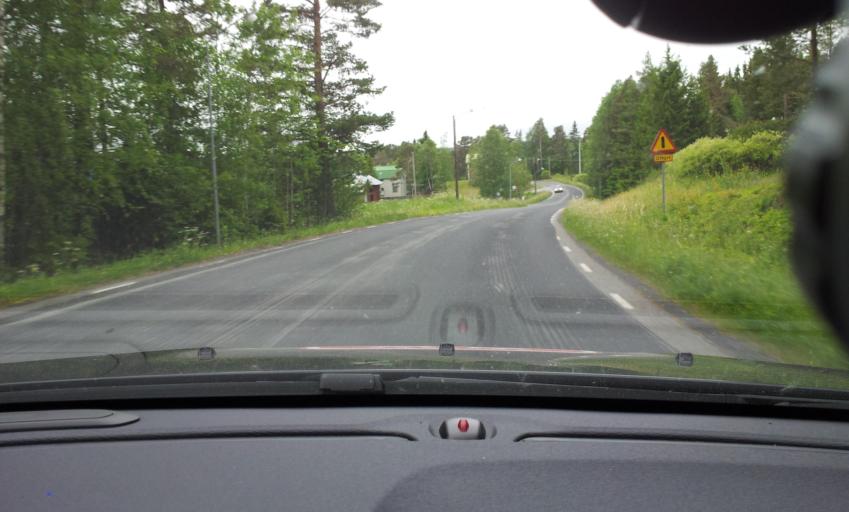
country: SE
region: Jaemtland
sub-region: Krokoms Kommun
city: Valla
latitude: 63.2837
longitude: 13.7716
